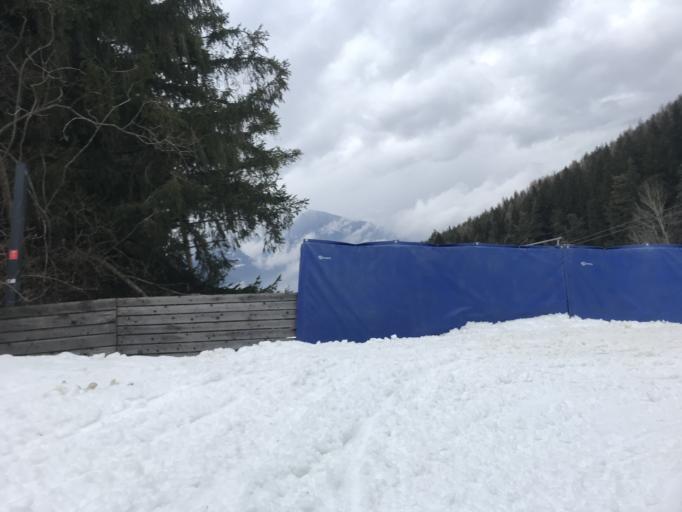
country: IT
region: Trentino-Alto Adige
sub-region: Bolzano
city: Bressanone
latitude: 46.6963
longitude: 11.6856
